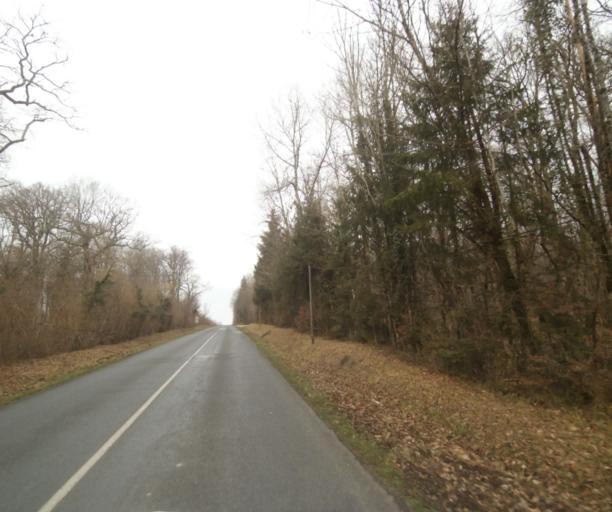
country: FR
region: Champagne-Ardenne
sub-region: Departement de la Haute-Marne
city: Villiers-en-Lieu
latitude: 48.6987
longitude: 4.8963
